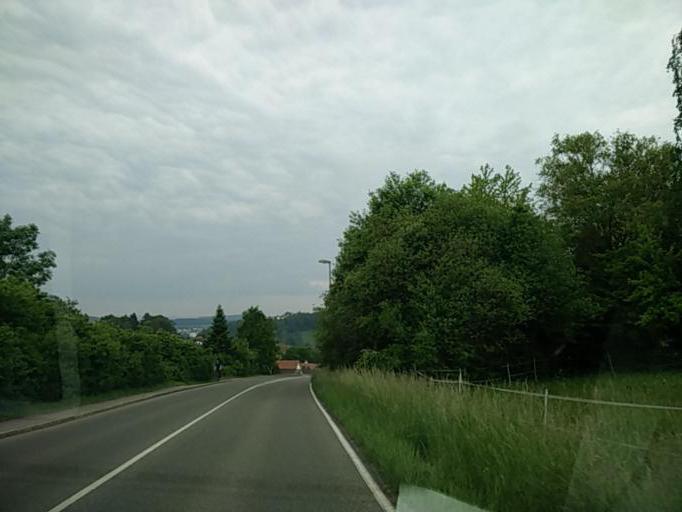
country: DE
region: Baden-Wuerttemberg
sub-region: Tuebingen Region
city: Kusterdingen
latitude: 48.5358
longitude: 9.0884
